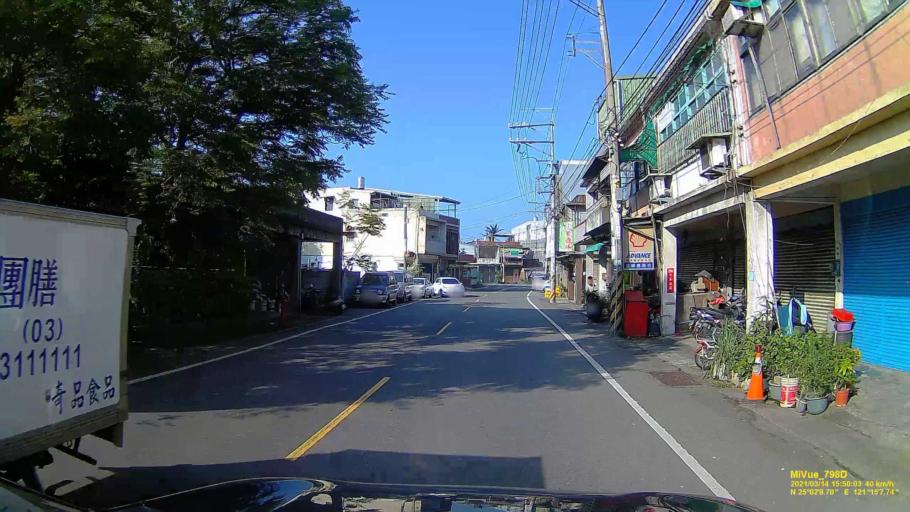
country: TW
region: Taiwan
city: Taoyuan City
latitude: 25.0362
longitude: 121.2522
